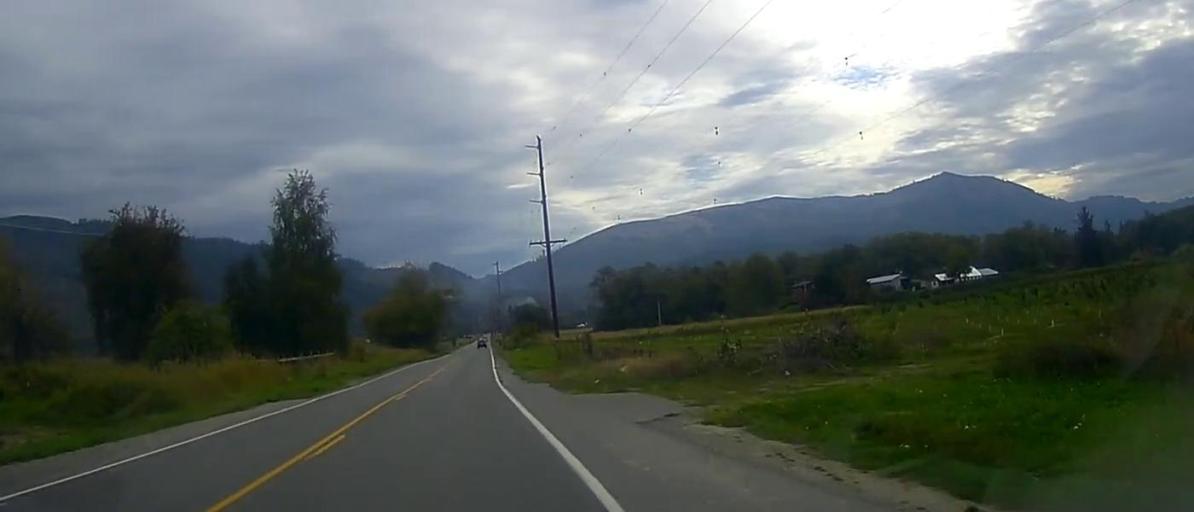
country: US
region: Washington
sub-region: Skagit County
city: Clear Lake
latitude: 48.4679
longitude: -122.2514
